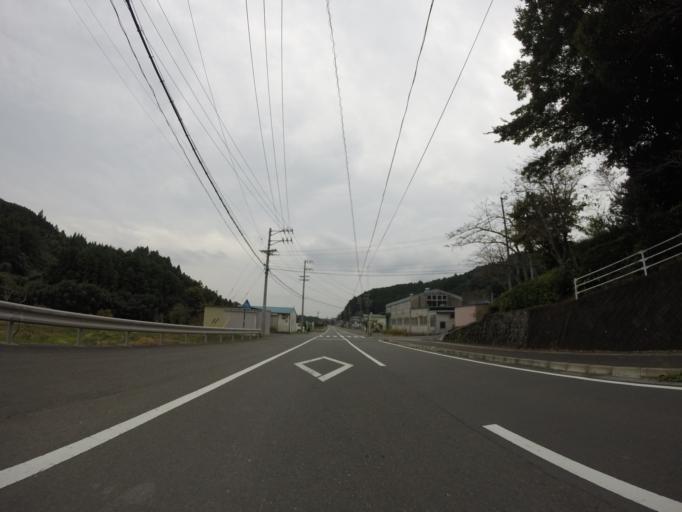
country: JP
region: Shizuoka
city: Kakegawa
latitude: 34.8172
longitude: 138.0184
